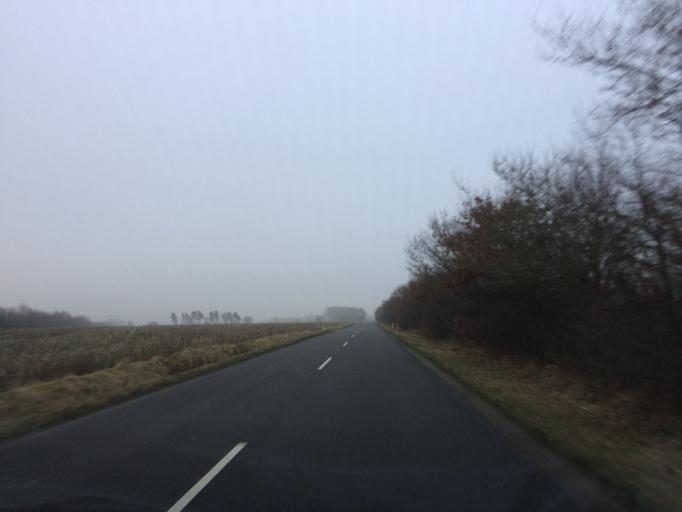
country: DK
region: South Denmark
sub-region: Varde Kommune
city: Oksbol
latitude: 55.6694
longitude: 8.3710
